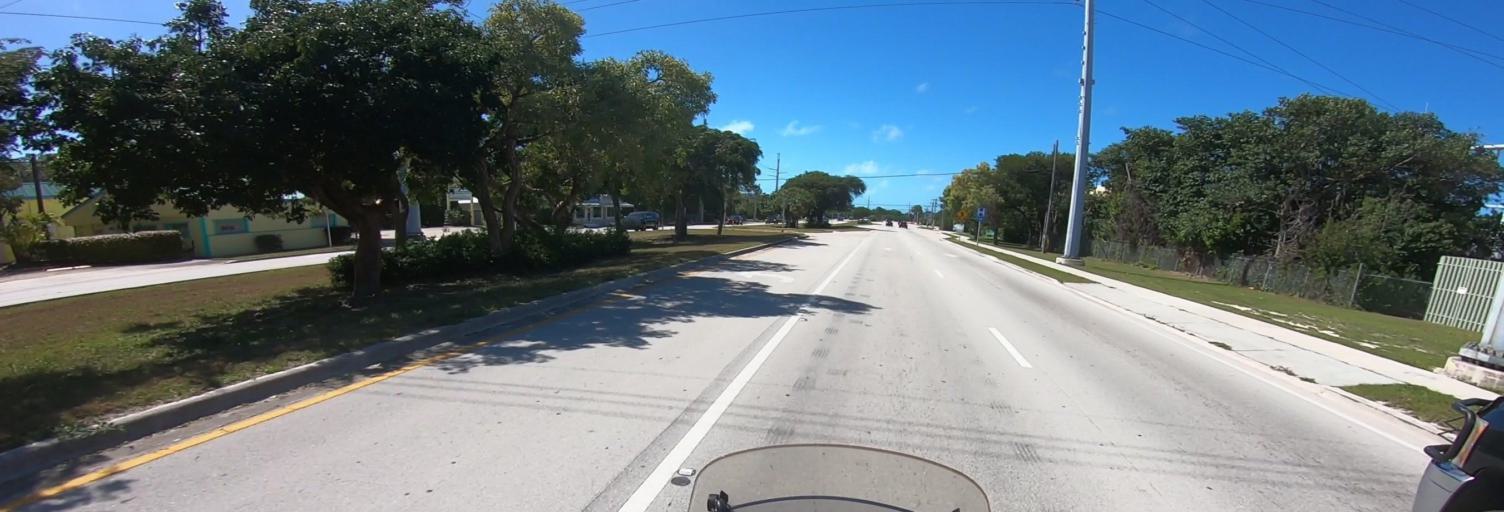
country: US
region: Florida
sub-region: Monroe County
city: Tavernier
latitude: 25.0064
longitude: -80.5210
